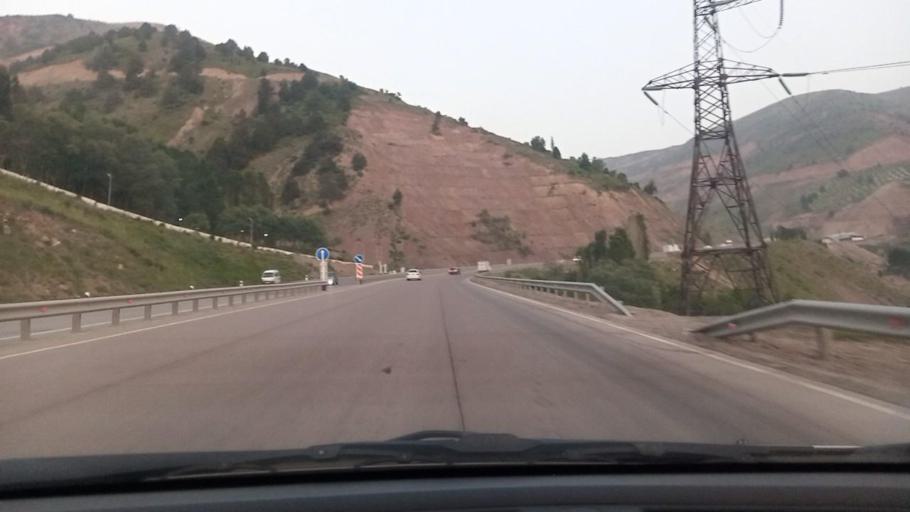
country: UZ
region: Toshkent
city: Angren
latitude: 41.1160
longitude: 70.4954
